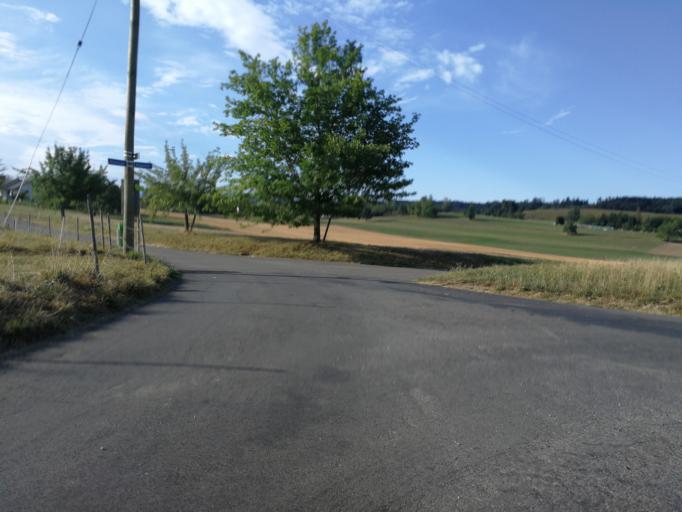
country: CH
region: Zurich
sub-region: Bezirk Meilen
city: Oetwil am See
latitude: 47.2727
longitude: 8.7377
